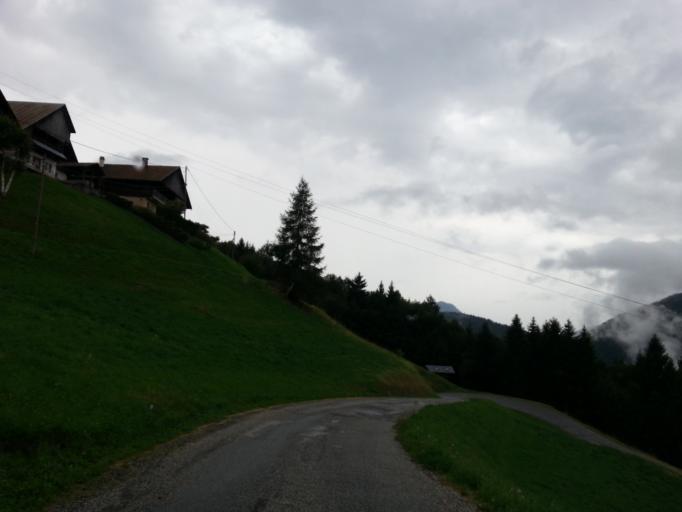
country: FR
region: Rhone-Alpes
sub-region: Departement de la Savoie
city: Marthod
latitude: 45.7100
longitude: 6.4650
